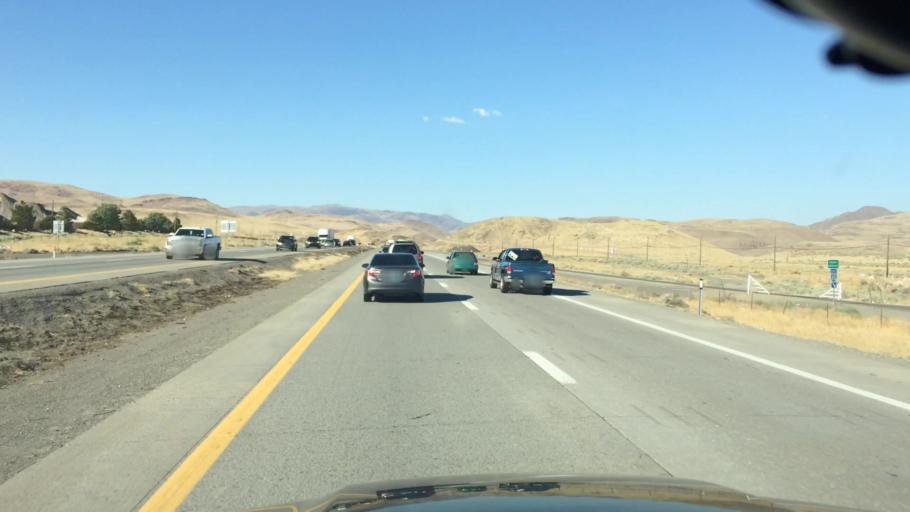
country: US
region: Nevada
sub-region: Washoe County
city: Sparks
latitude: 39.5211
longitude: -119.6266
